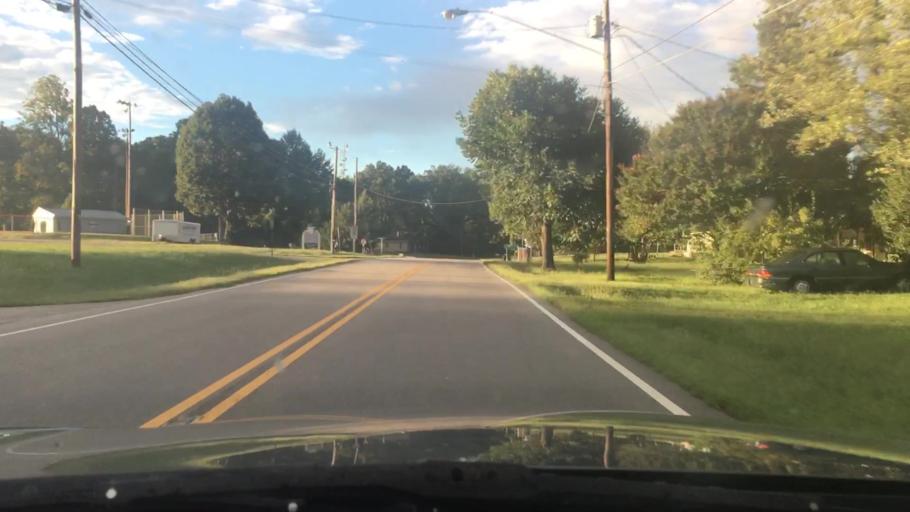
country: US
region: North Carolina
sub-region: Caswell County
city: Yanceyville
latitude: 36.4022
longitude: -79.3292
